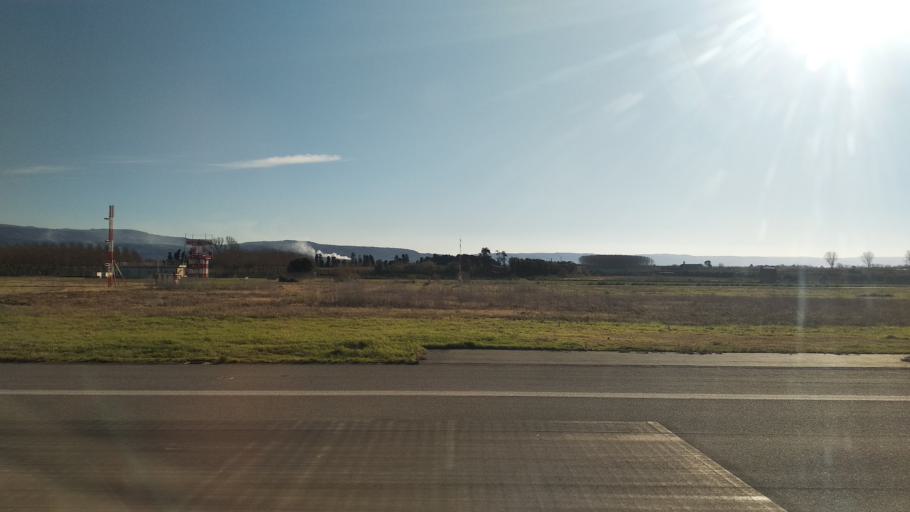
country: IT
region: Calabria
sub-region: Provincia di Catanzaro
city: Santa Eufemia Lamezia
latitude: 38.9045
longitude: 16.2503
